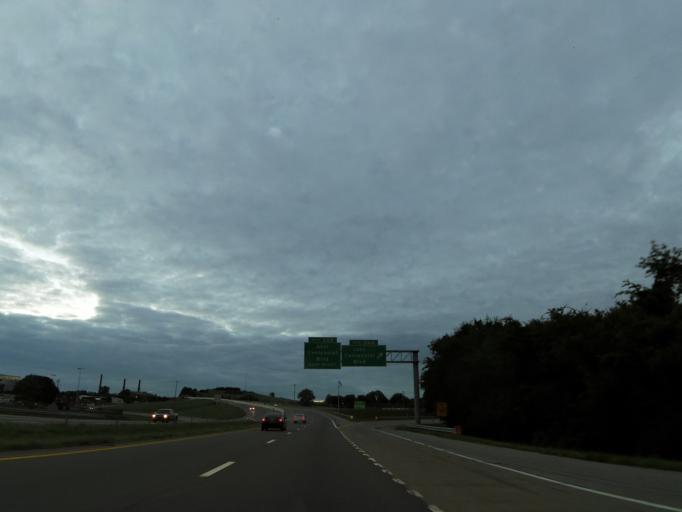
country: US
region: Tennessee
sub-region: Davidson County
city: Belle Meade
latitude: 36.1678
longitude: -86.8696
